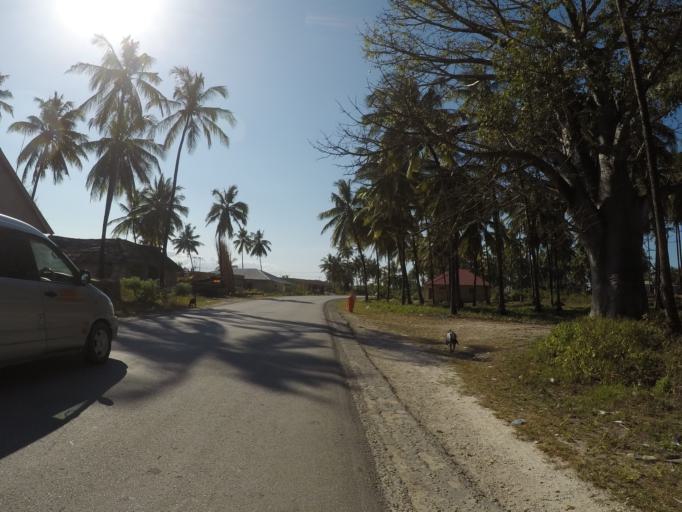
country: TZ
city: Kiwengwa
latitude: -6.1490
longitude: 39.5154
